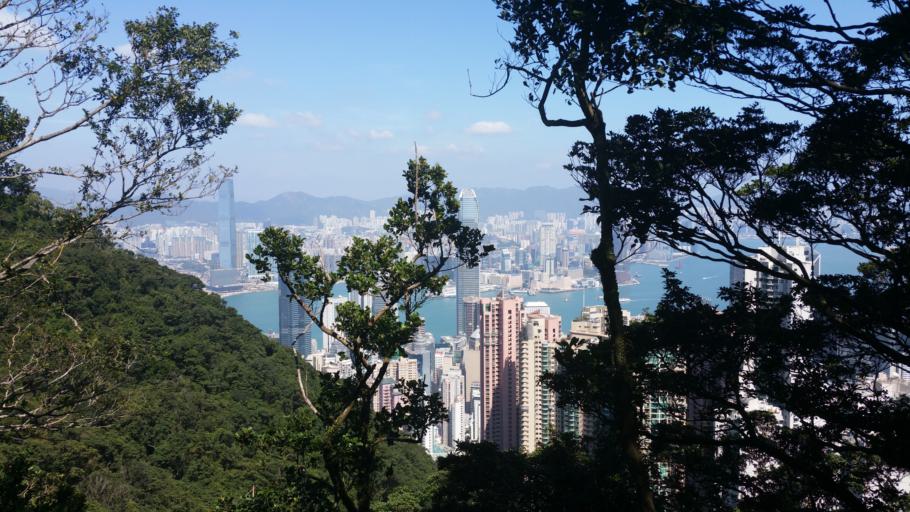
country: HK
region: Central and Western
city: Central
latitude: 22.2727
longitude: 114.1493
